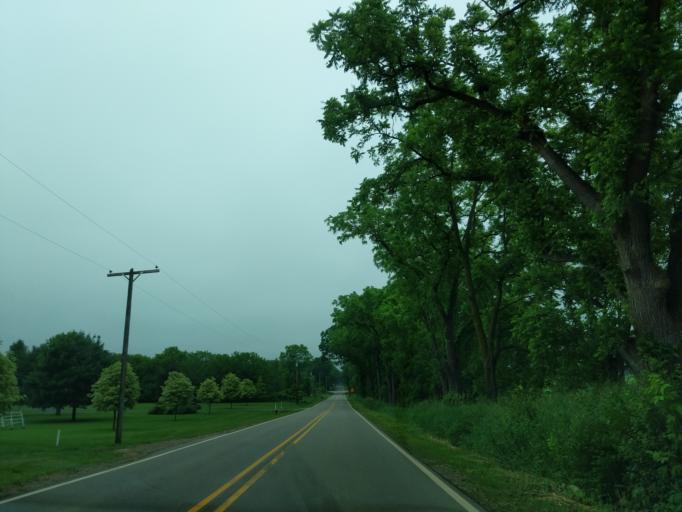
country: US
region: Michigan
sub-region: Jackson County
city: Spring Arbor
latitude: 42.2049
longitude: -84.5700
